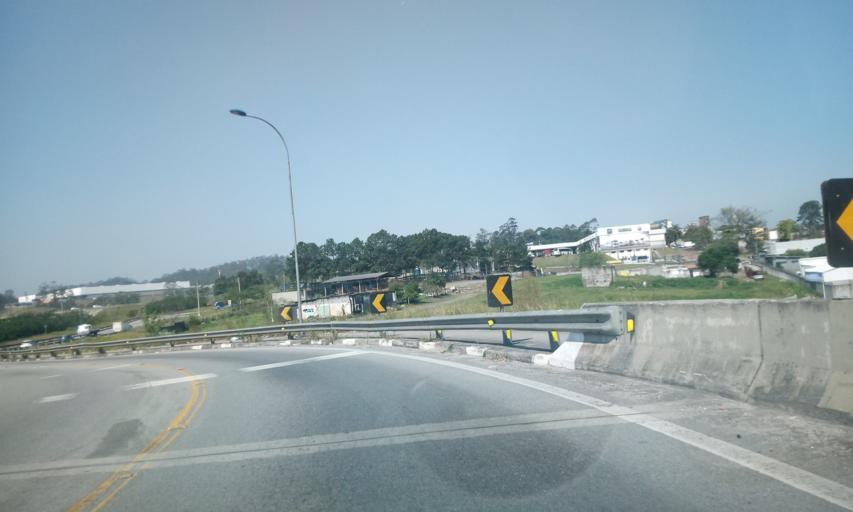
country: BR
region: Sao Paulo
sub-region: Sao Bernardo Do Campo
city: Sao Bernardo do Campo
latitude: -23.7659
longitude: -46.5956
